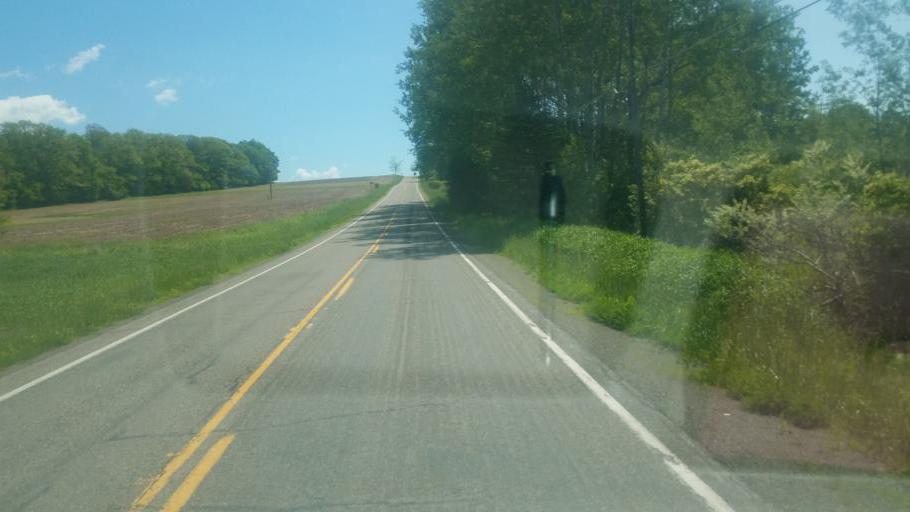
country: US
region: Pennsylvania
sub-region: Tioga County
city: Wellsboro
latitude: 41.7334
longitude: -77.3704
